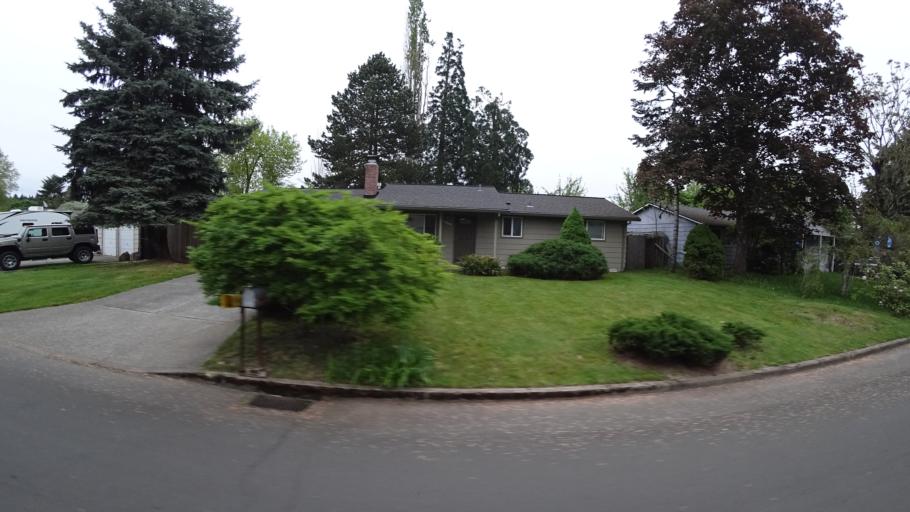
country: US
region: Oregon
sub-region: Washington County
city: Aloha
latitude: 45.5057
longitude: -122.8794
